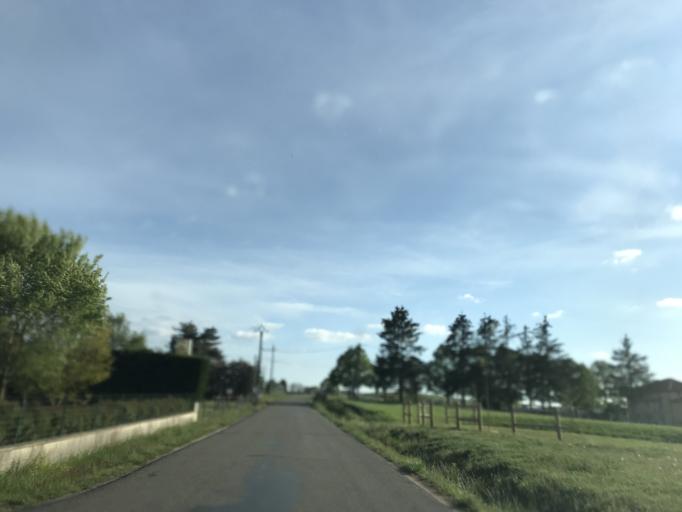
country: FR
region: Auvergne
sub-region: Departement du Puy-de-Dome
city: Courpiere
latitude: 45.7189
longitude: 3.4674
